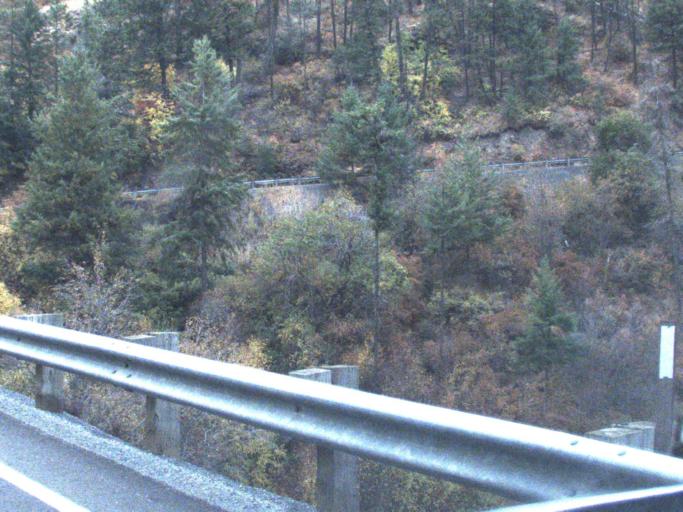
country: US
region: Washington
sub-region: Okanogan County
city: Coulee Dam
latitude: 47.8718
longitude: -118.7195
